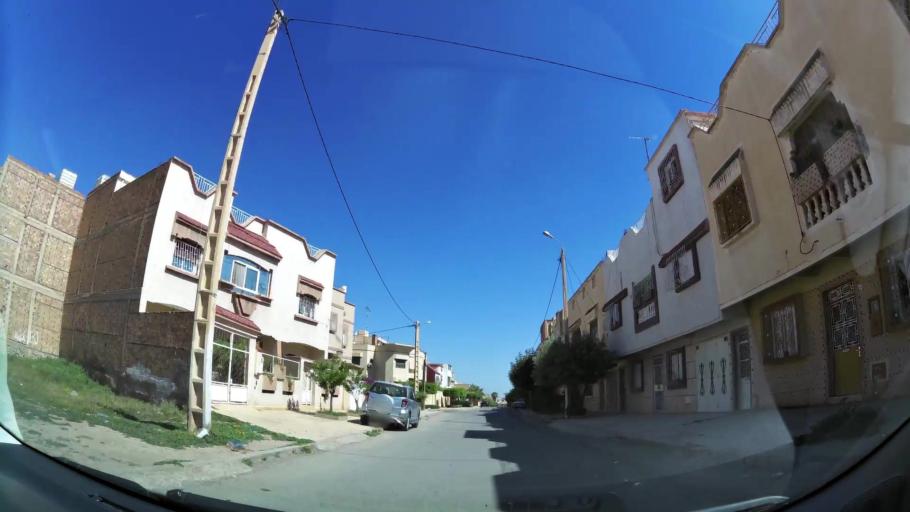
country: MA
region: Oriental
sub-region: Oujda-Angad
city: Oujda
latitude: 34.6618
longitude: -1.8932
